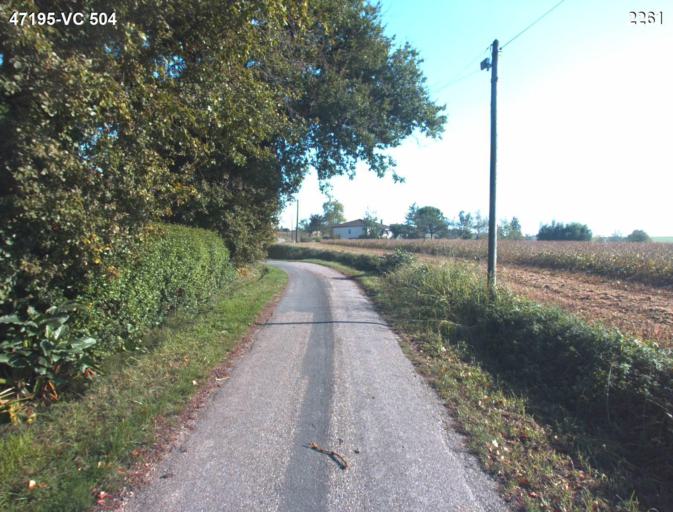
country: FR
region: Aquitaine
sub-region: Departement du Lot-et-Garonne
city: Nerac
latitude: 44.1657
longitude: 0.3382
